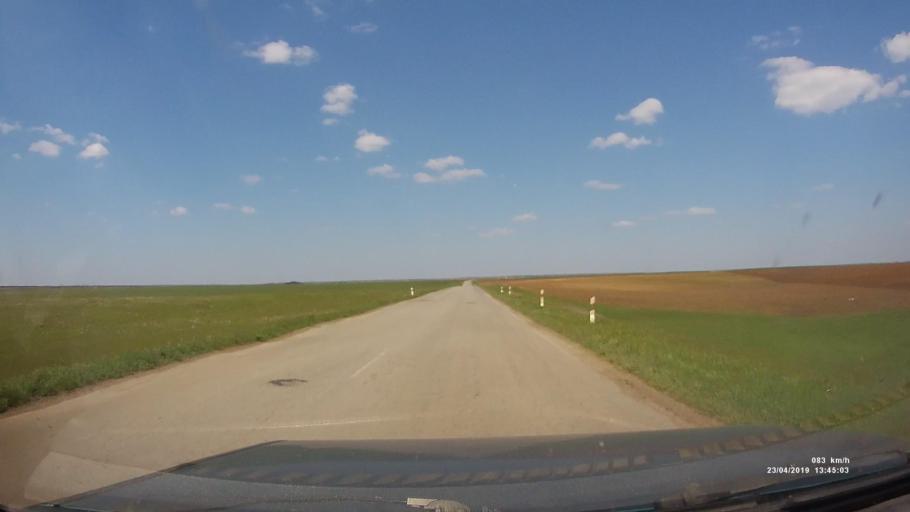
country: RU
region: Kalmykiya
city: Yashalta
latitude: 46.5882
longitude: 42.8200
